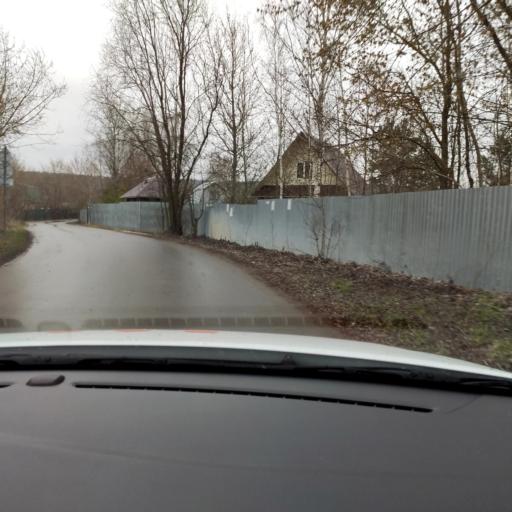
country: RU
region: Tatarstan
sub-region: Gorod Kazan'
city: Kazan
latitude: 55.6916
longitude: 49.0711
